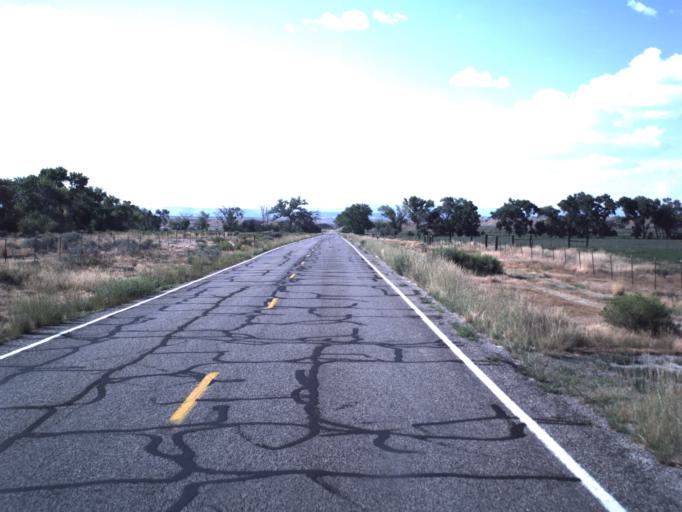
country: US
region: Utah
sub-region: Emery County
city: Huntington
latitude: 39.4217
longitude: -110.8590
